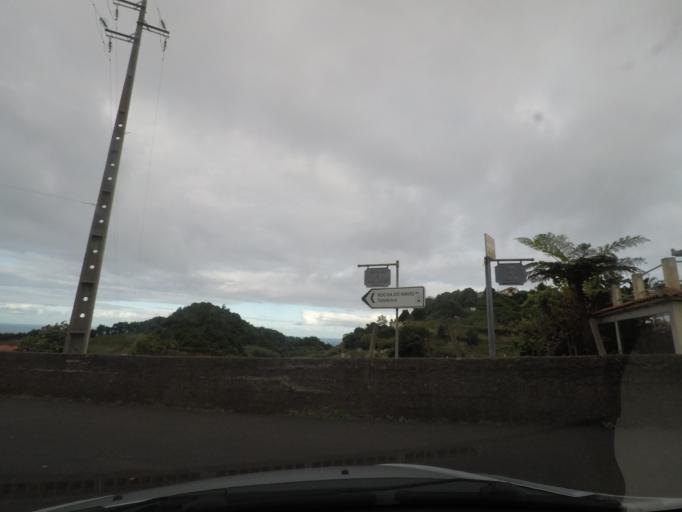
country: PT
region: Madeira
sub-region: Santana
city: Santana
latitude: 32.8123
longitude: -16.8796
